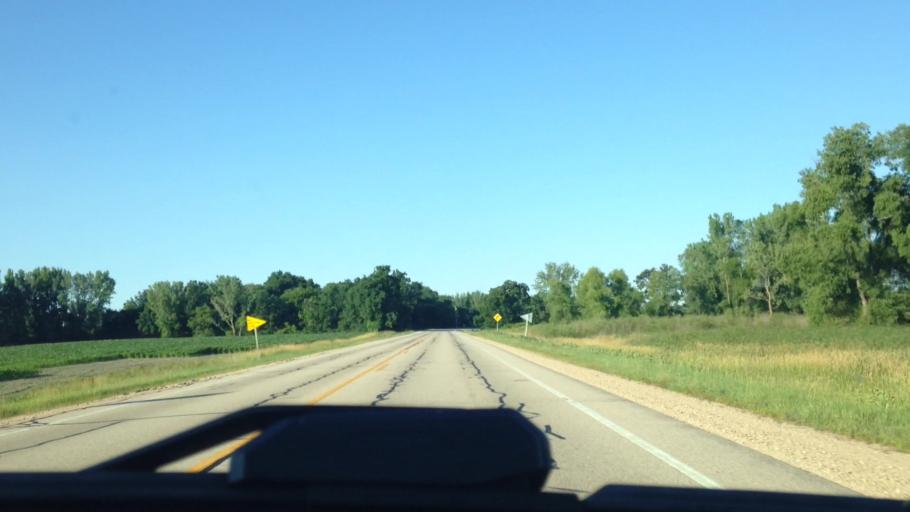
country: US
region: Wisconsin
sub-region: Columbia County
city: Rio
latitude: 43.3370
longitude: -89.2574
